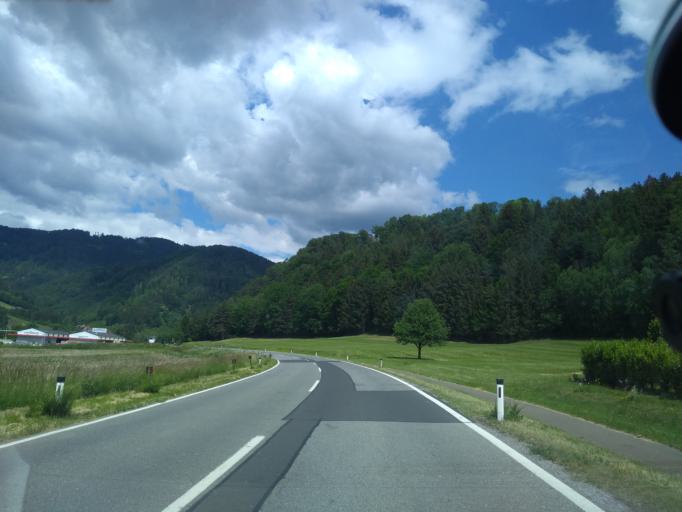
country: AT
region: Styria
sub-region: Politischer Bezirk Graz-Umgebung
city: Frohnleiten
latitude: 47.2451
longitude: 15.3216
